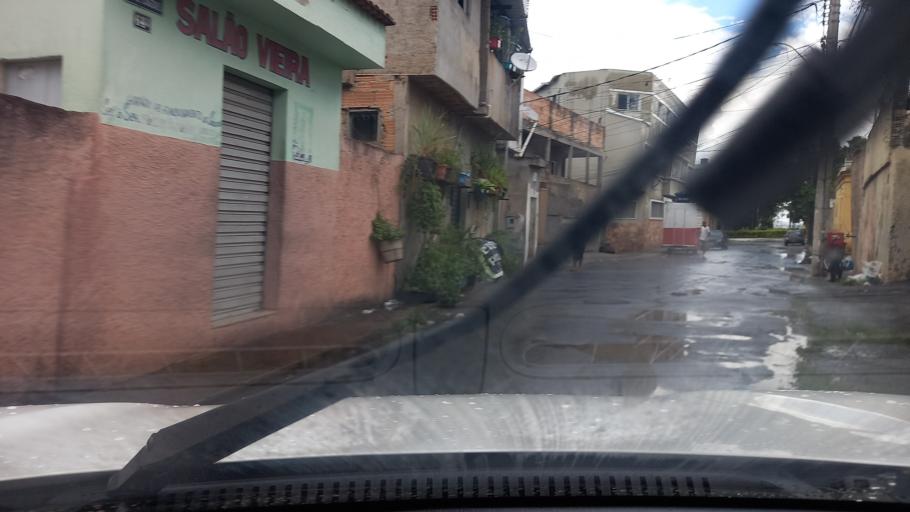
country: BR
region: Minas Gerais
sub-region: Belo Horizonte
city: Belo Horizonte
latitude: -19.9064
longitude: -43.9503
